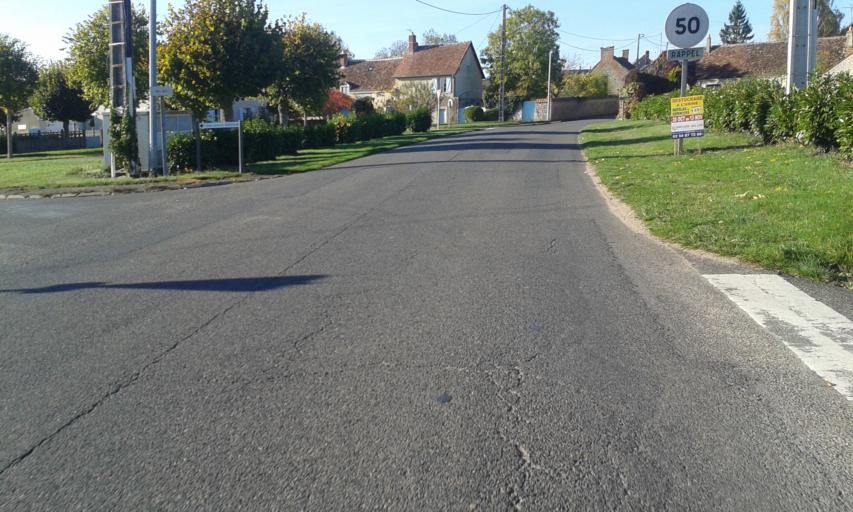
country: FR
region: Centre
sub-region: Departement du Loir-et-Cher
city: Oucques
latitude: 47.8296
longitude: 1.3832
